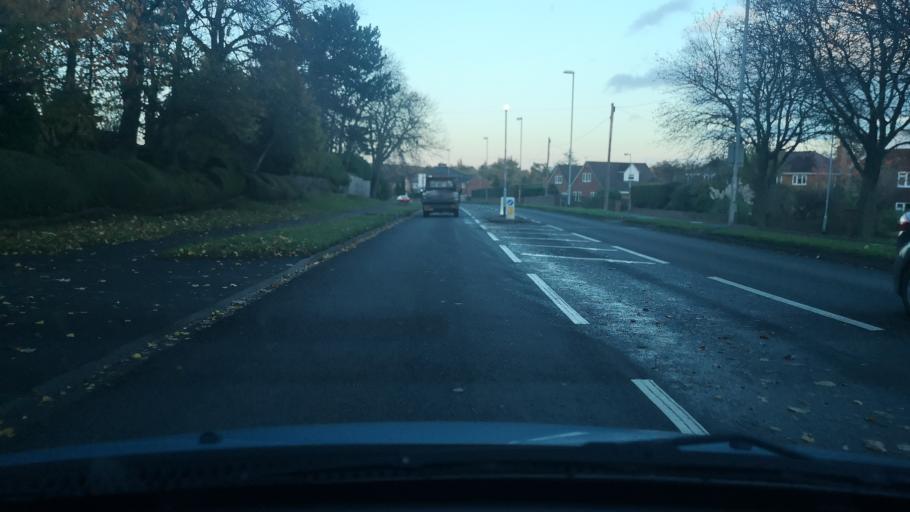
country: GB
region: England
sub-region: City and Borough of Wakefield
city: Horbury
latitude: 53.6628
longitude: -1.5429
